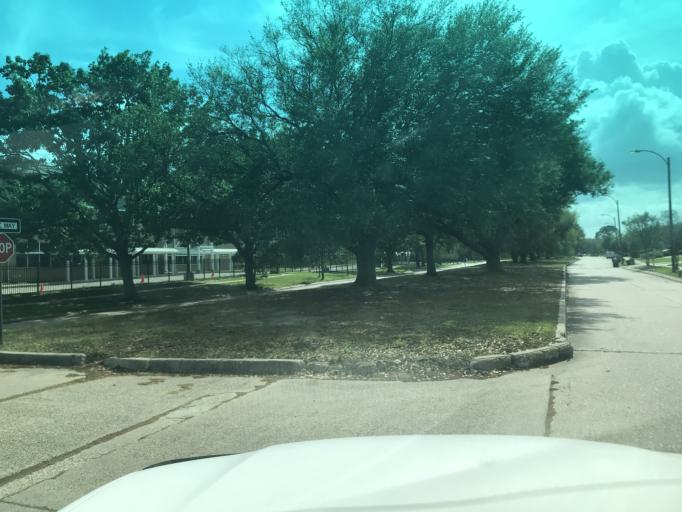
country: US
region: Louisiana
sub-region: Saint Bernard Parish
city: Chalmette
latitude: 30.0362
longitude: -89.9593
